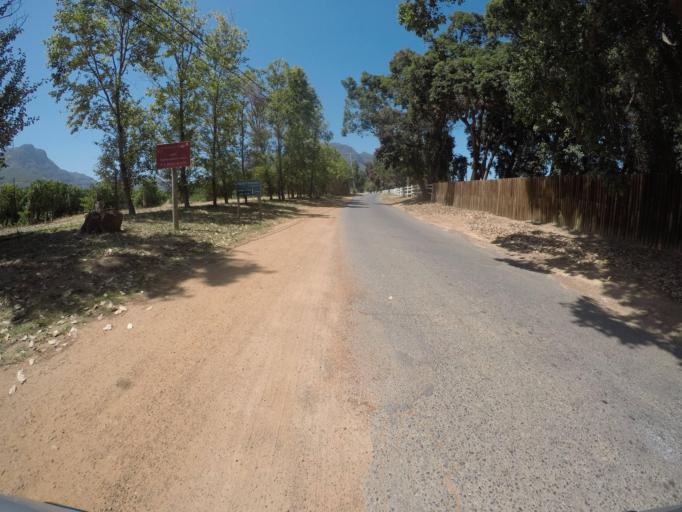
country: ZA
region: Western Cape
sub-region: Cape Winelands District Municipality
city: Stellenbosch
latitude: -33.9904
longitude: 18.8681
